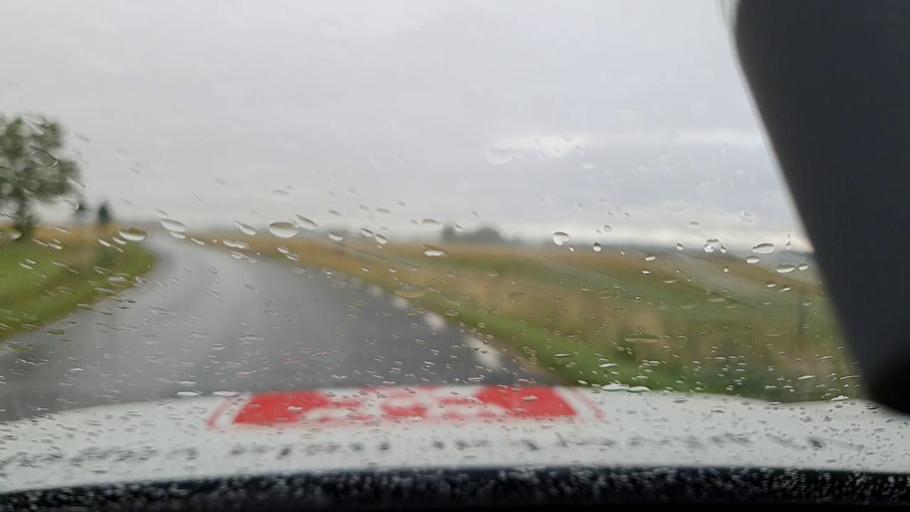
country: SE
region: Vaestra Goetaland
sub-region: Toreboda Kommun
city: Toereboda
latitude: 58.6525
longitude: 14.1061
